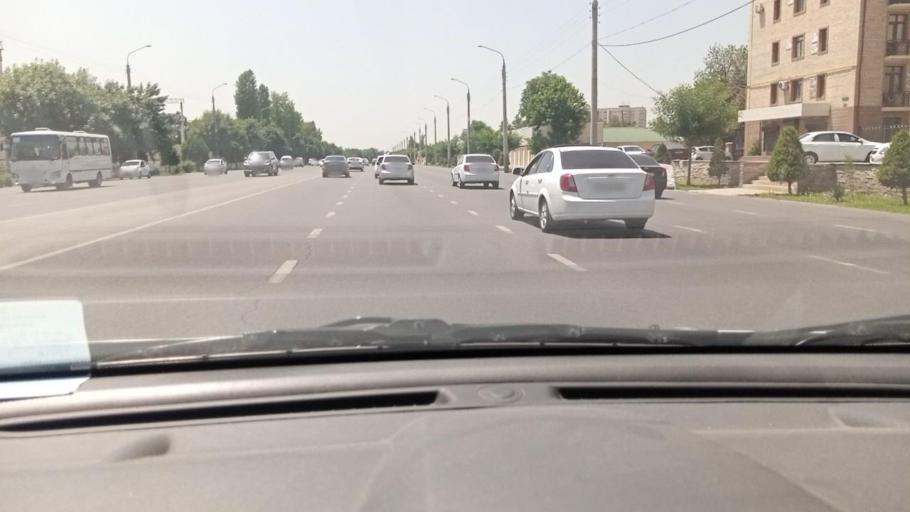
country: UZ
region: Toshkent Shahri
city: Tashkent
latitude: 41.2768
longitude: 69.2715
